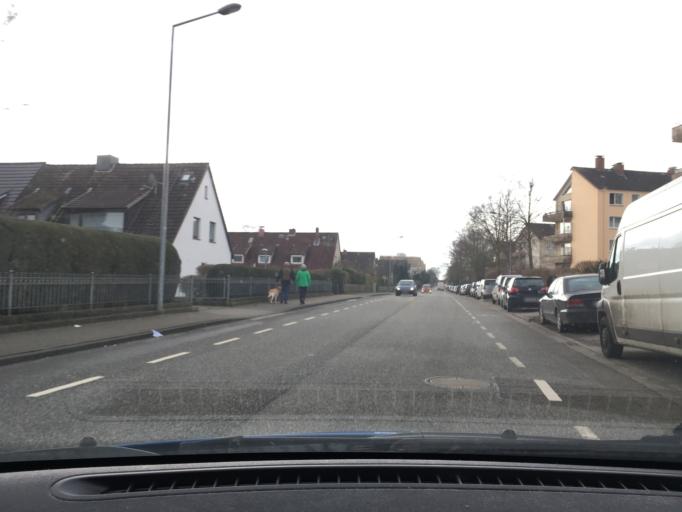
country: DE
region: Schleswig-Holstein
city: Wedel
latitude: 53.5777
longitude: 9.7278
